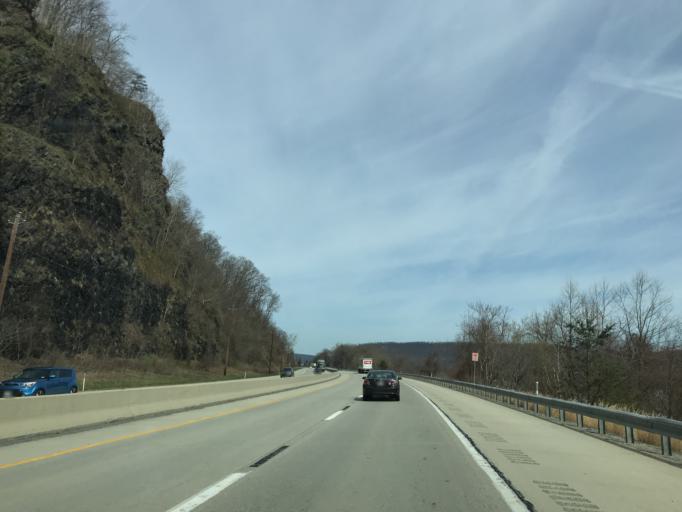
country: US
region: Pennsylvania
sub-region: Dauphin County
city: Matamoras
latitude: 40.4837
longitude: -76.9495
